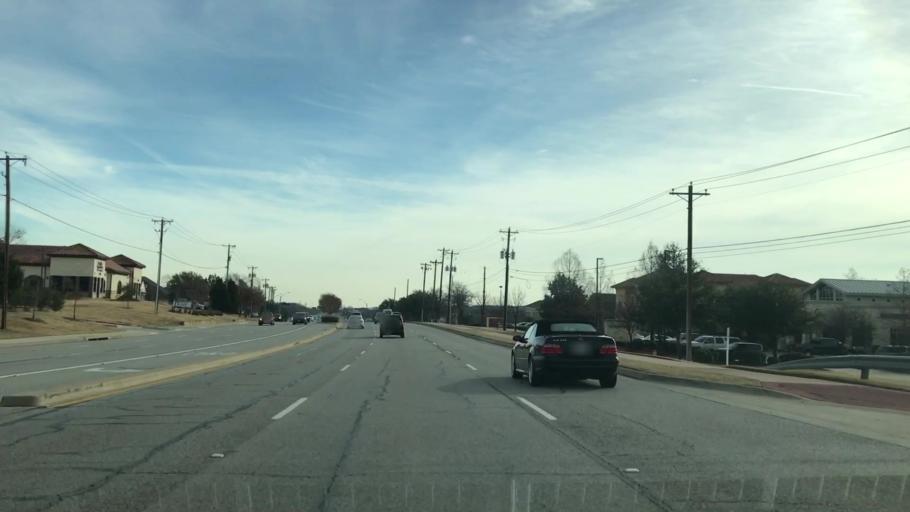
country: US
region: Texas
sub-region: Tarrant County
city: Southlake
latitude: 32.9410
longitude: -97.1464
